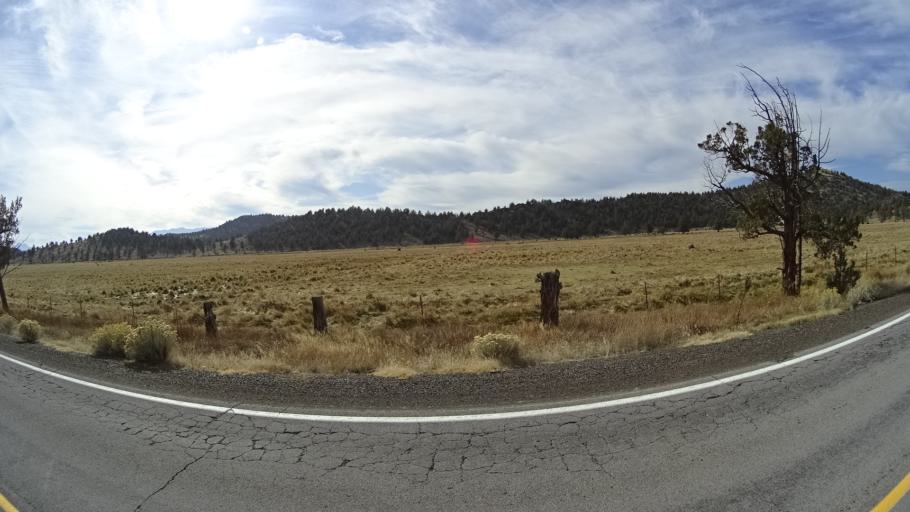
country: US
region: California
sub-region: Siskiyou County
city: Weed
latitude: 41.5736
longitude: -122.3928
